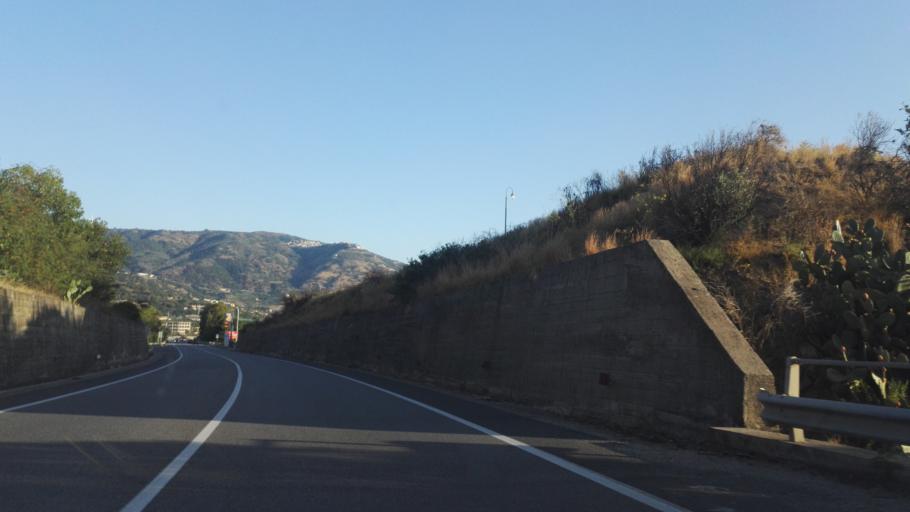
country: IT
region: Calabria
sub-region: Provincia di Catanzaro
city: Soverato Superiore
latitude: 38.6982
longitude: 16.5372
